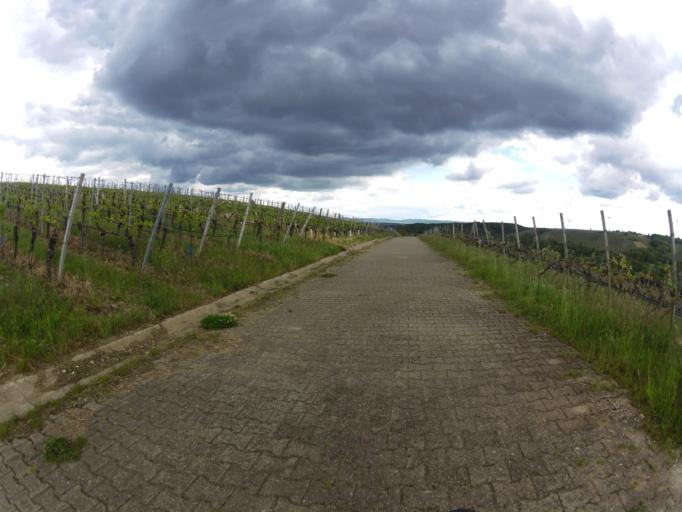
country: DE
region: Bavaria
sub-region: Regierungsbezirk Unterfranken
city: Sommerach
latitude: 49.8394
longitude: 10.1846
